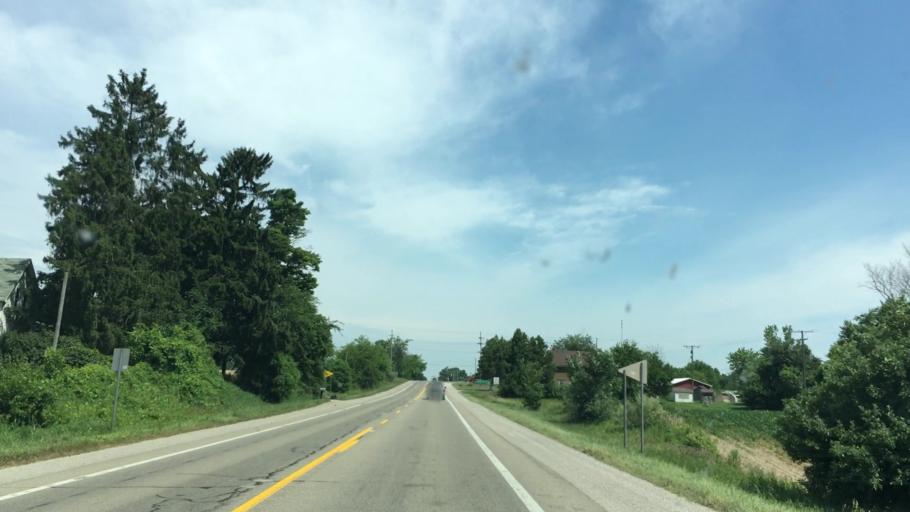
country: US
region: Michigan
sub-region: Lapeer County
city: Imlay City
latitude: 43.0992
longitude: -83.0718
